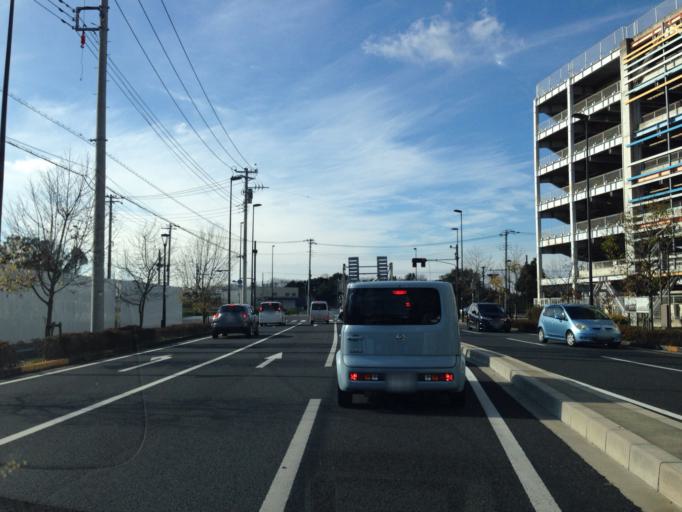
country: JP
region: Chiba
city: Kashiwa
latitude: 35.8920
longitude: 139.9512
